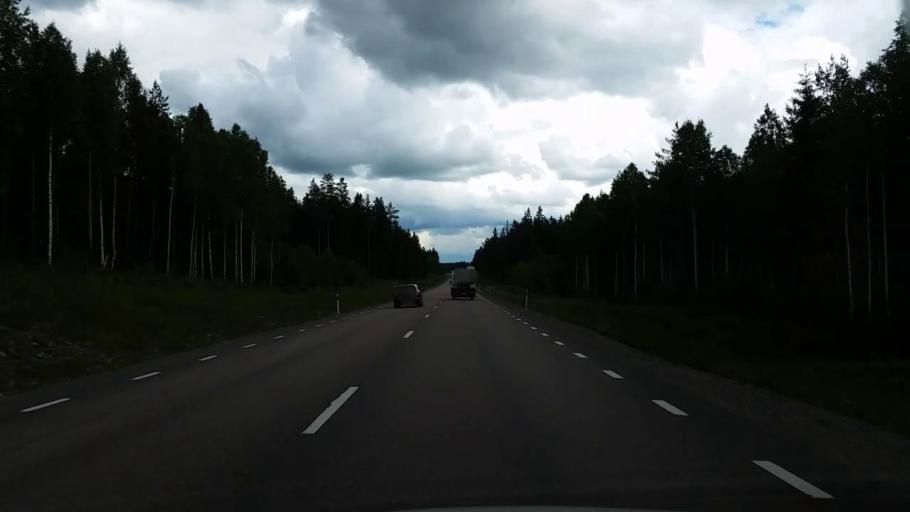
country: SE
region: Dalarna
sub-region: Avesta Kommun
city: Horndal
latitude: 60.4567
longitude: 16.4454
